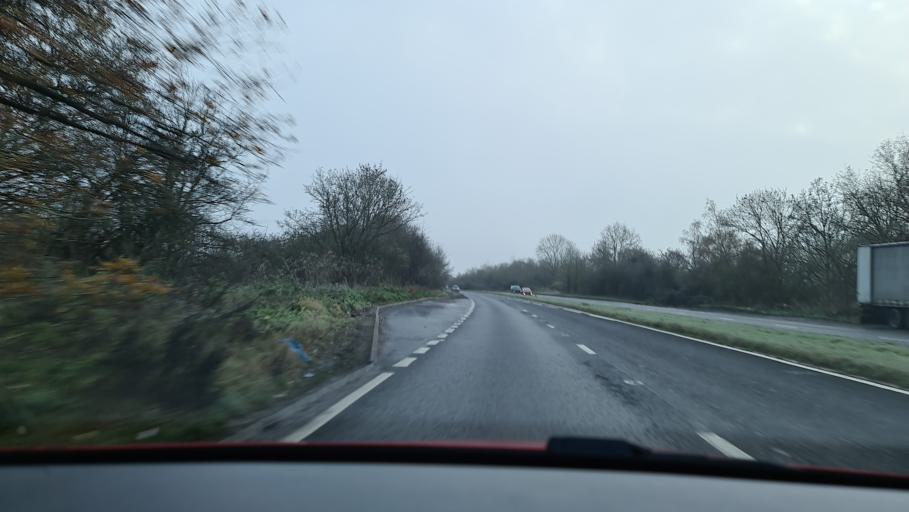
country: GB
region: England
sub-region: Buckinghamshire
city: Seer Green
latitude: 51.5996
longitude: -0.6199
